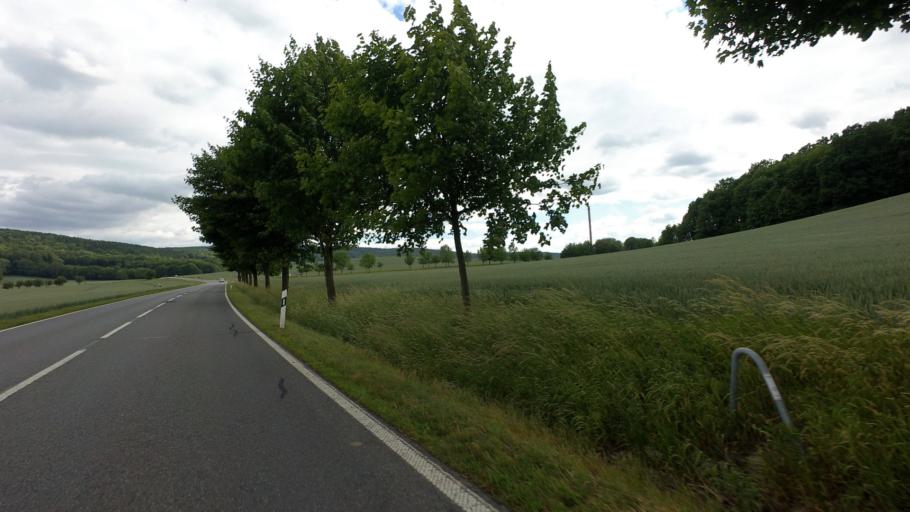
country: DE
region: Saxony
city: Neustadt in Sachsen
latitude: 51.0185
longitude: 14.2324
